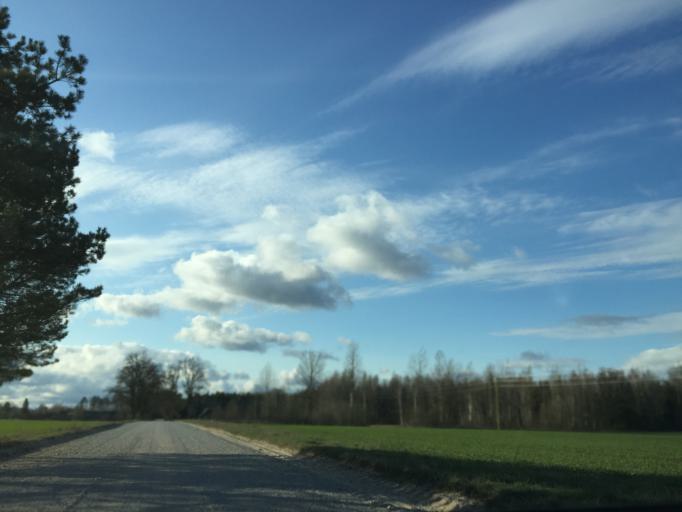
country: LV
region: Burtnieki
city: Matisi
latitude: 57.6195
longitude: 25.0715
